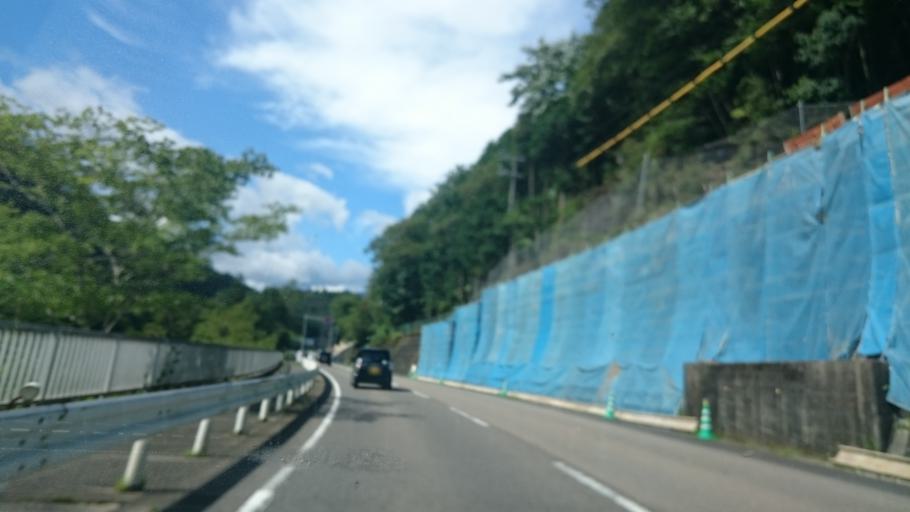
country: JP
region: Gifu
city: Nakatsugawa
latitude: 35.6001
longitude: 137.4644
